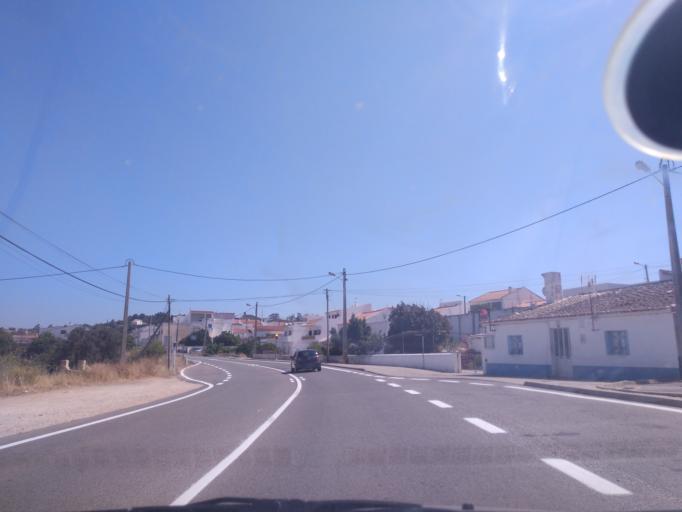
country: PT
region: Faro
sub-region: Lagos
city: Lagos
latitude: 37.1258
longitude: -8.6953
